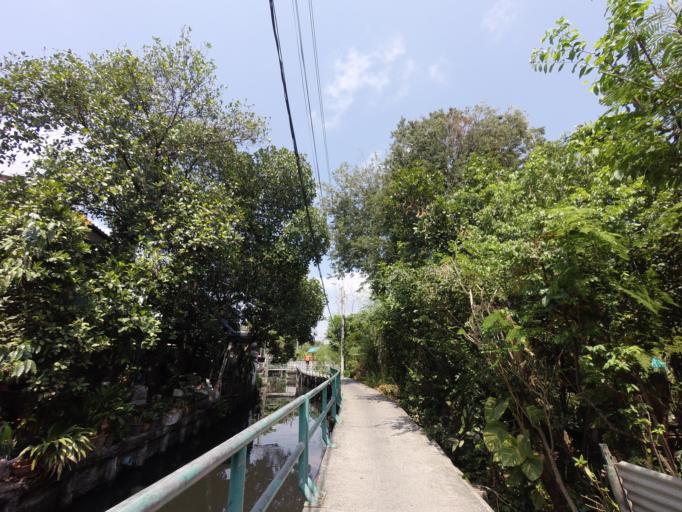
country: TH
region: Bangkok
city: Rat Burana
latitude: 13.6630
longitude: 100.5084
